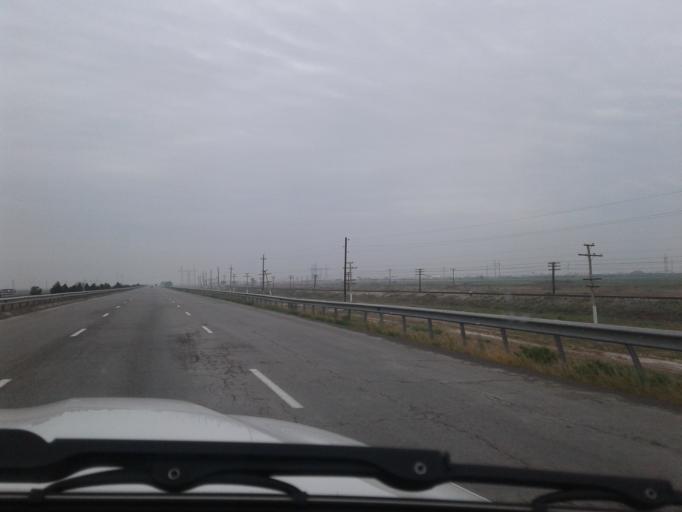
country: TM
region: Mary
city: Bayramaly
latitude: 37.6209
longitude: 62.0638
